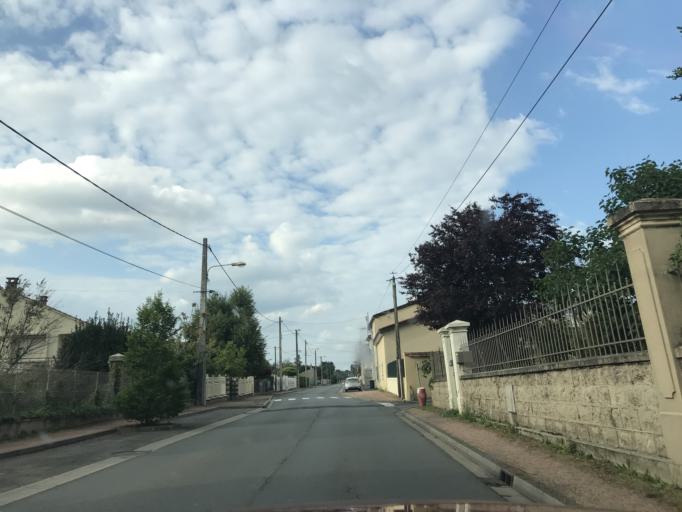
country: FR
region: Auvergne
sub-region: Departement du Puy-de-Dome
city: Lezoux
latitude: 45.8333
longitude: 3.3845
